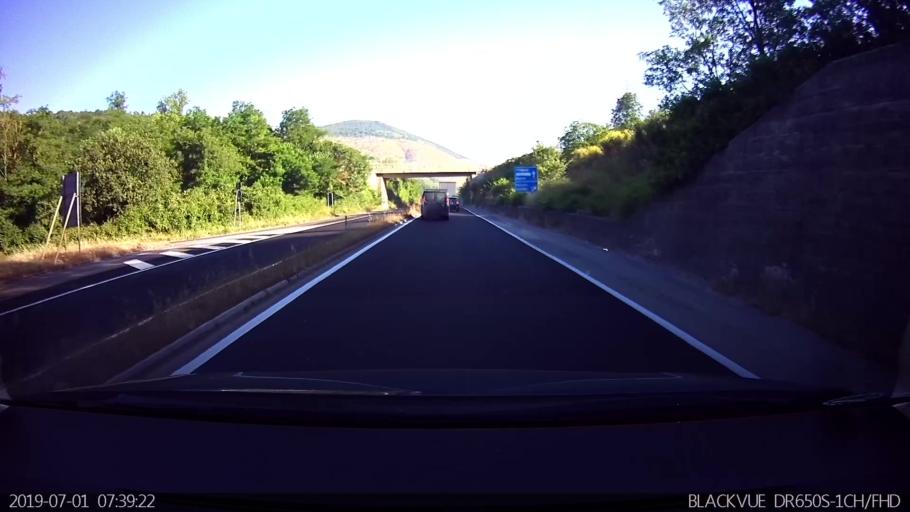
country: IT
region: Latium
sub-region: Provincia di Frosinone
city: Giuliano di Roma
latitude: 41.5490
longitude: 13.2688
